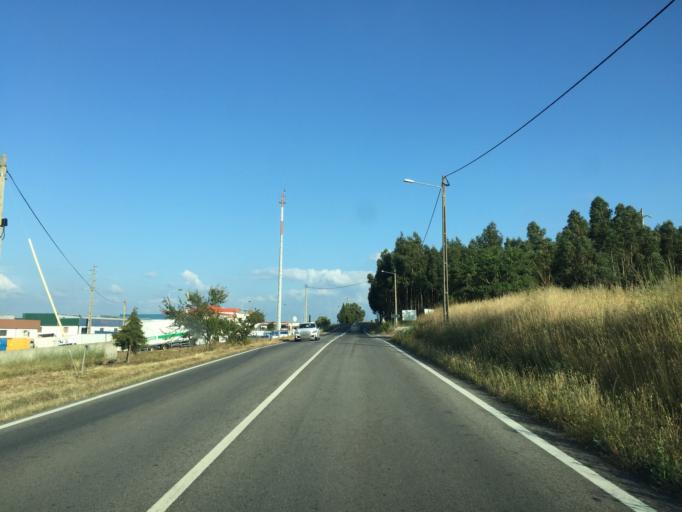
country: PT
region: Lisbon
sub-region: Alenquer
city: Alenquer
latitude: 39.1290
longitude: -8.9934
